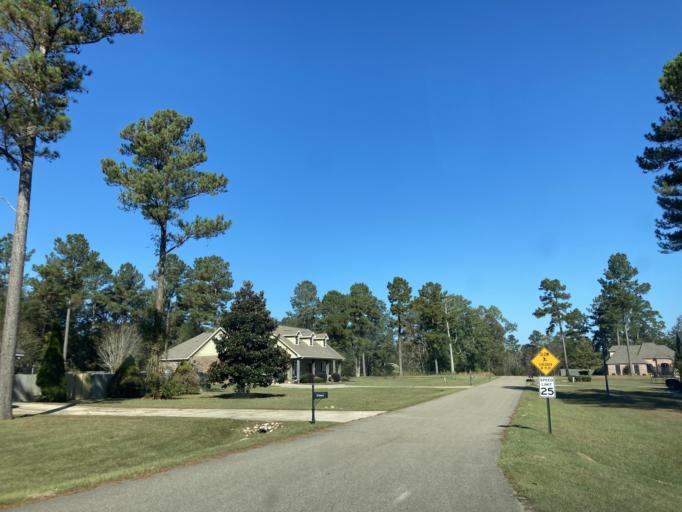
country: US
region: Mississippi
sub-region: Lamar County
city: Sumrall
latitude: 31.3475
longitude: -89.4957
